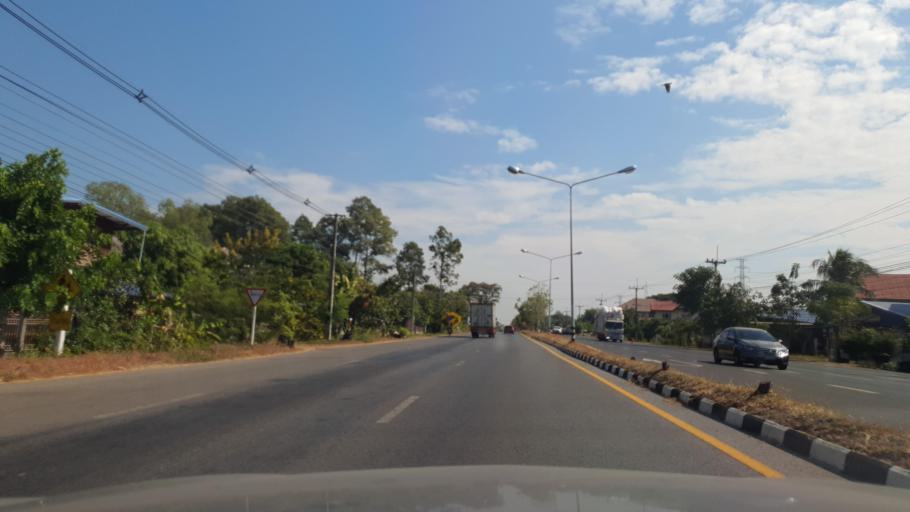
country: TH
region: Maha Sarakham
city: Kantharawichai
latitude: 16.3865
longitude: 103.2442
